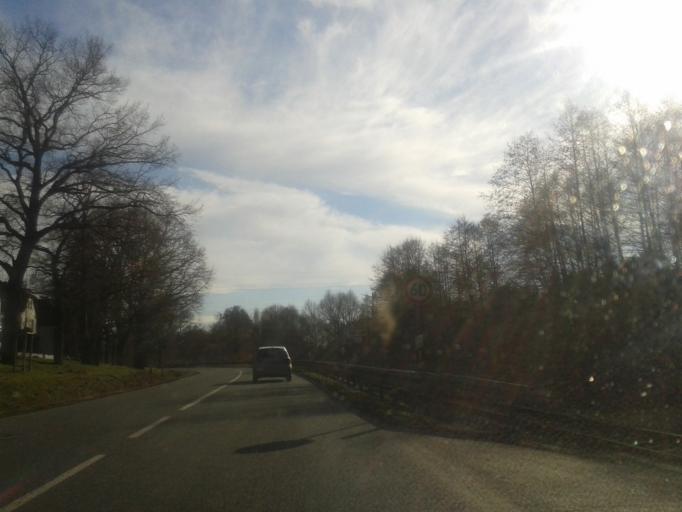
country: DE
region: Saxony
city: Ottendorf-Okrilla
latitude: 51.1593
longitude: 13.8071
